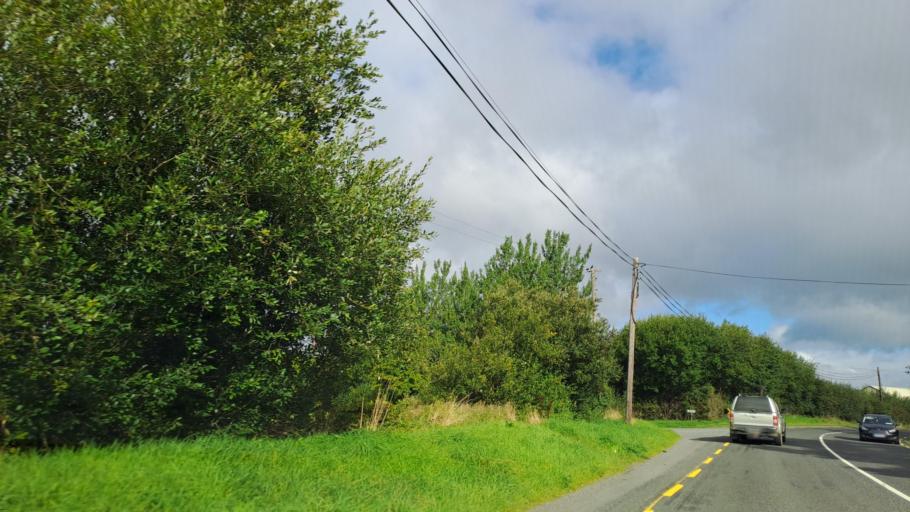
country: IE
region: Ulster
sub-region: County Monaghan
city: Carrickmacross
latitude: 53.9526
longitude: -6.7591
